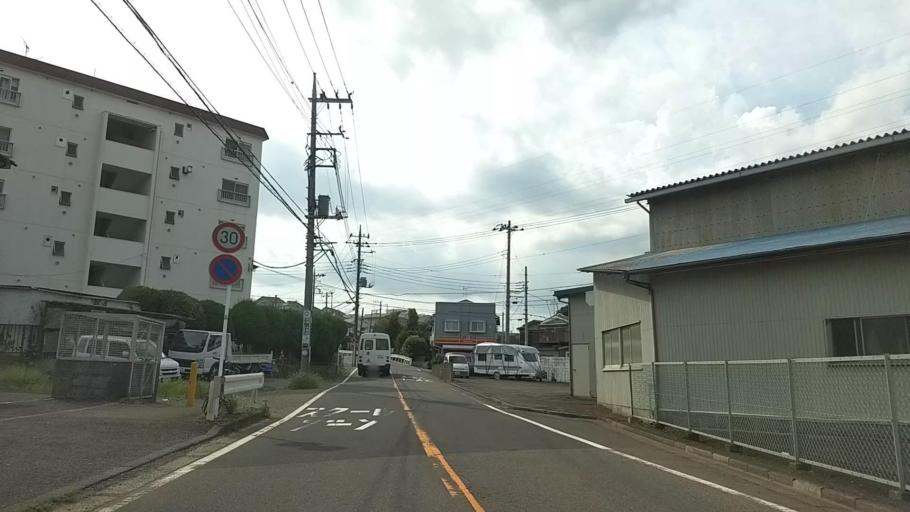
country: JP
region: Kanagawa
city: Yokohama
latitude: 35.4903
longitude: 139.5791
